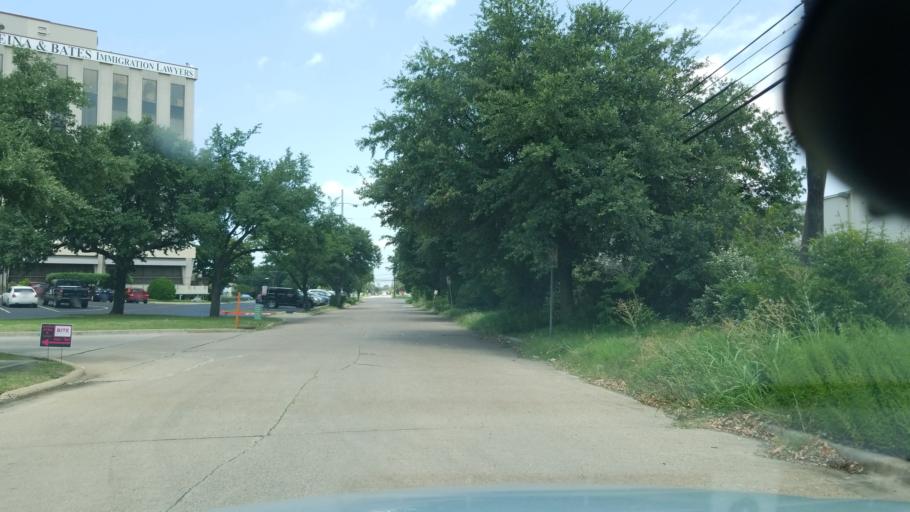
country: US
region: Texas
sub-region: Dallas County
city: Irving
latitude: 32.8242
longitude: -96.8741
